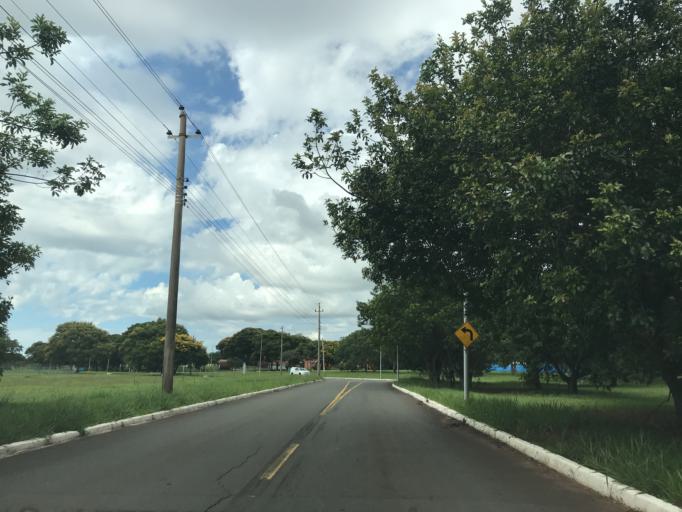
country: BR
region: Federal District
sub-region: Brasilia
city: Brasilia
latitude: -15.8075
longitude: -47.8777
